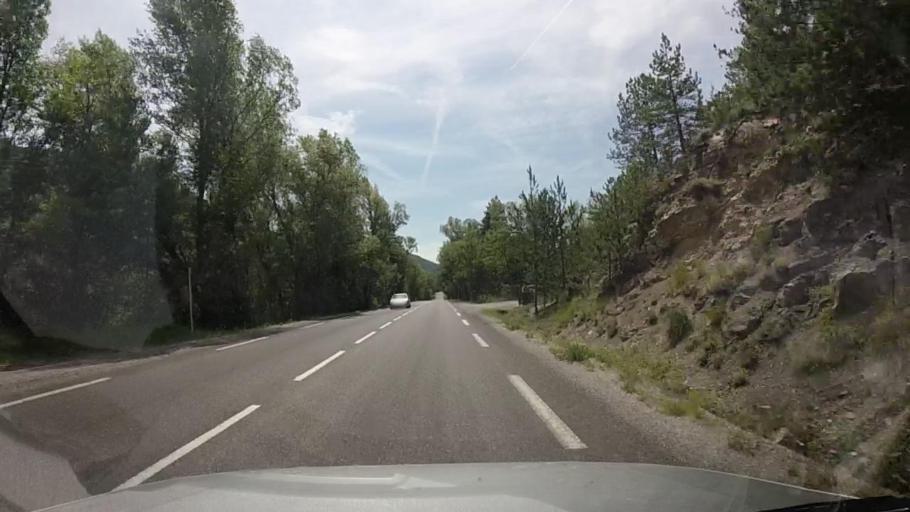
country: FR
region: Provence-Alpes-Cote d'Azur
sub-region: Departement des Alpes-de-Haute-Provence
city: Digne-les-Bains
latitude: 44.1120
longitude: 6.2665
